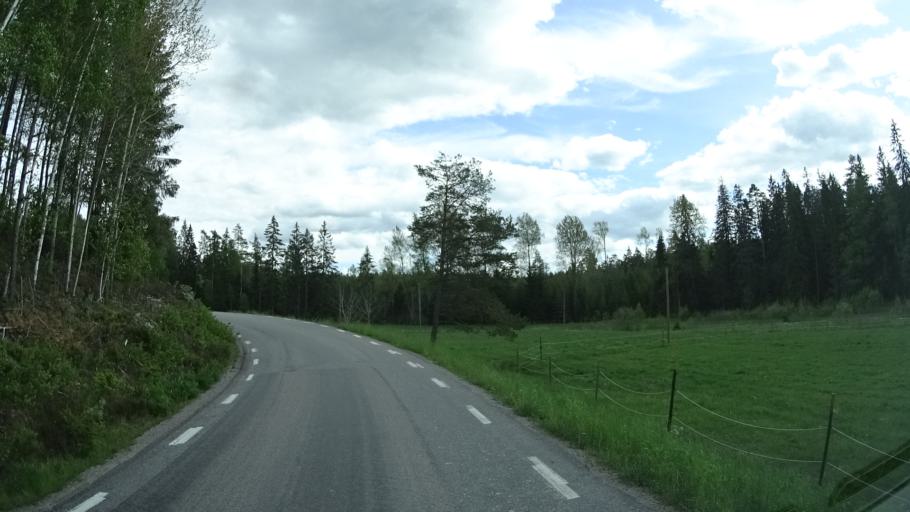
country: SE
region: OEstergoetland
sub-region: Finspangs Kommun
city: Finspang
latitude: 58.6053
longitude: 15.7493
